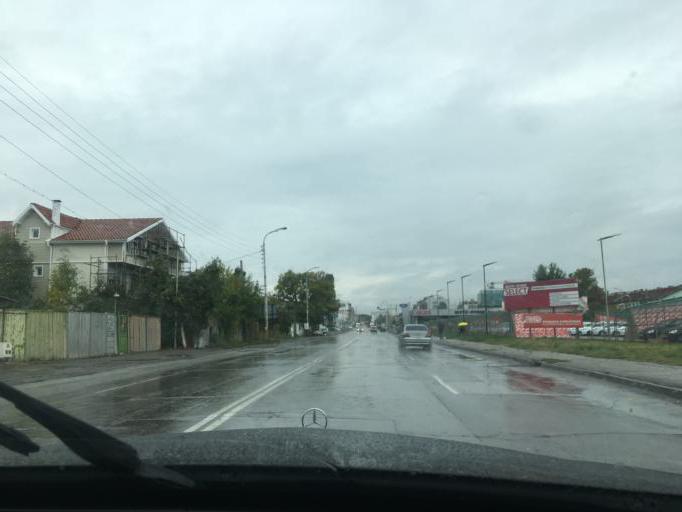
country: BG
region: Sofiya
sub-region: Obshtina Bozhurishte
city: Bozhurishte
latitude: 42.7288
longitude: 23.2583
